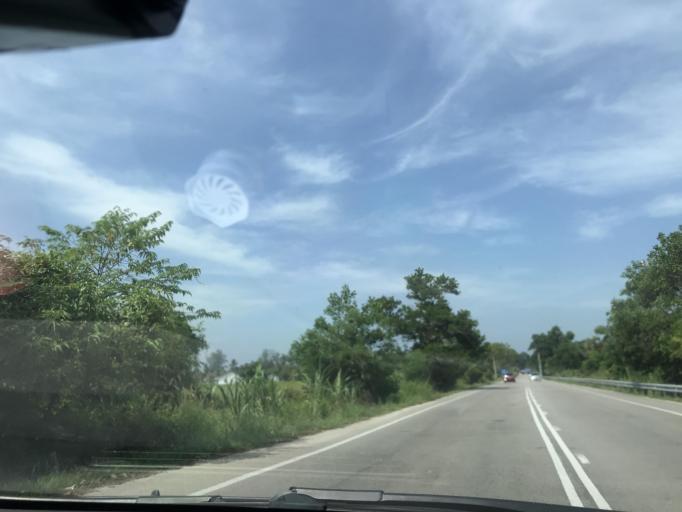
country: MY
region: Kelantan
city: Tumpat
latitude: 6.1963
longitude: 102.1552
